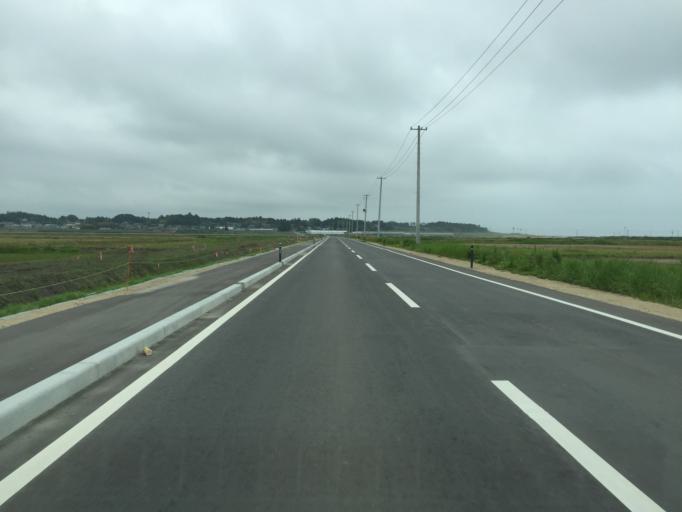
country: JP
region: Fukushima
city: Namie
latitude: 37.6970
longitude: 141.0058
